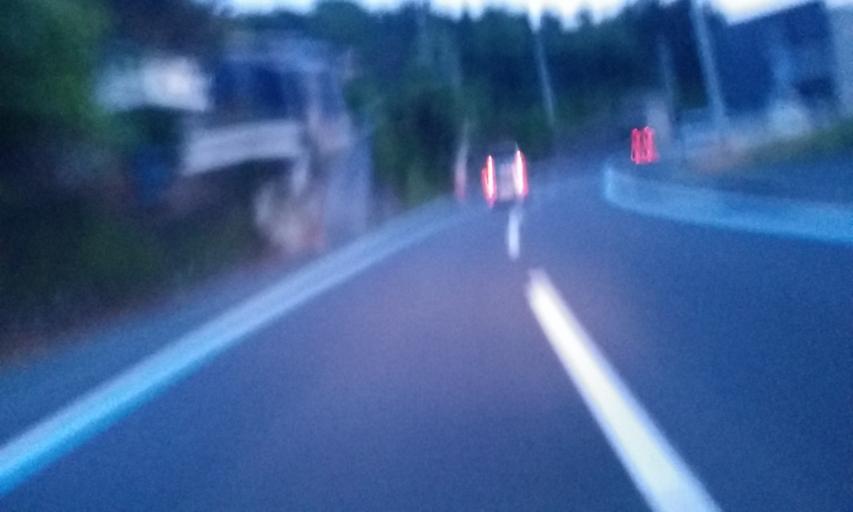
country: JP
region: Ehime
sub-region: Nishiuwa-gun
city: Ikata-cho
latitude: 33.5057
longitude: 132.3981
